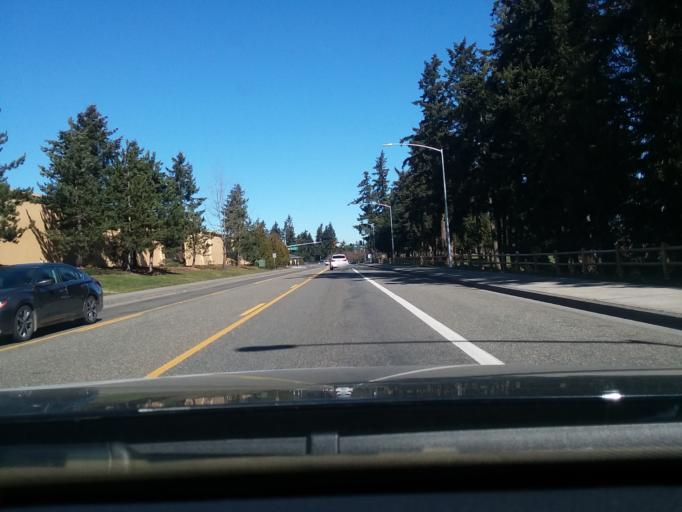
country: US
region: Washington
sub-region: Pierce County
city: Puyallup
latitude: 47.1605
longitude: -122.2877
